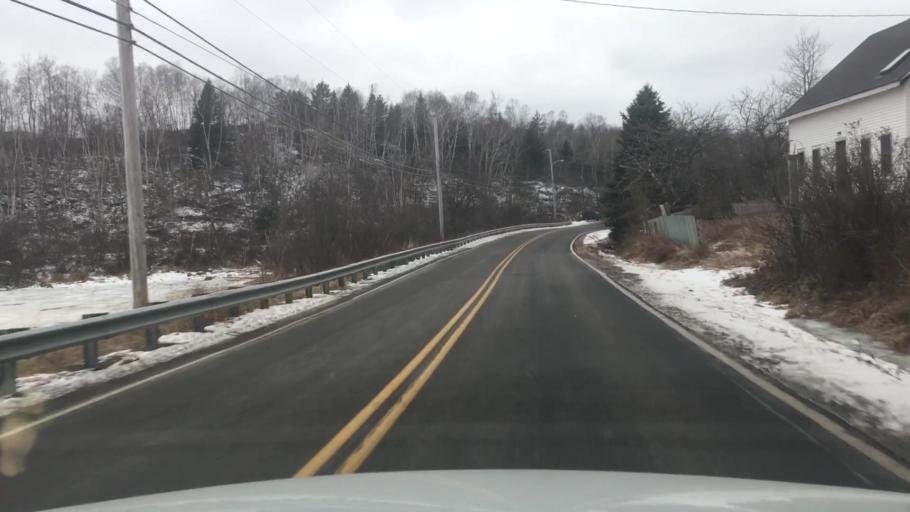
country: US
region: Maine
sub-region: Washington County
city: East Machias
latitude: 44.7247
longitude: -67.3853
